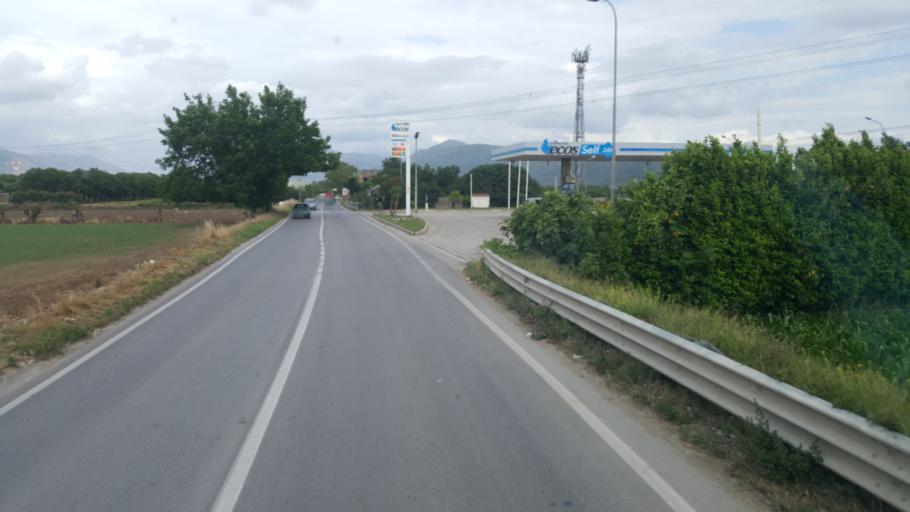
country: IT
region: Campania
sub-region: Provincia di Caserta
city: Maddaloni
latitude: 41.0089
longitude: 14.3883
